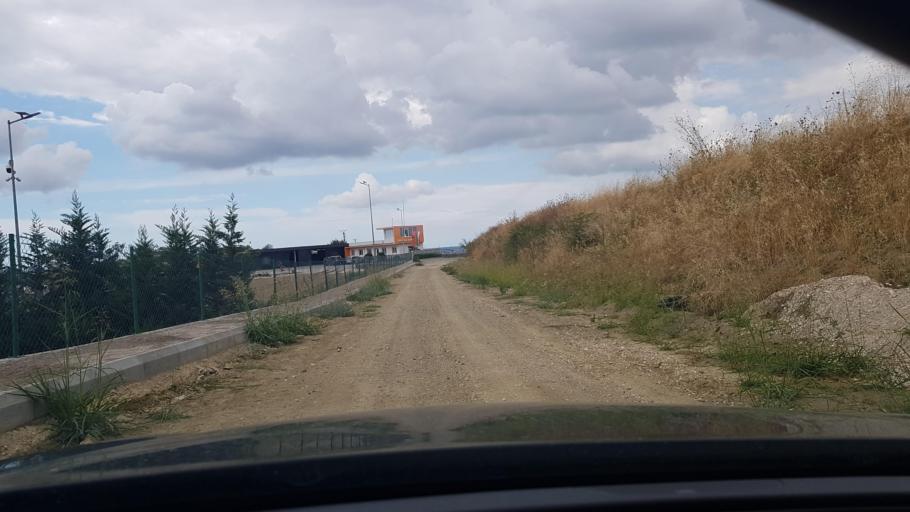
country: AL
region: Durres
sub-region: Rrethi i Durresit
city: Gjepalaj
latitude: 41.3019
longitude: 19.5531
